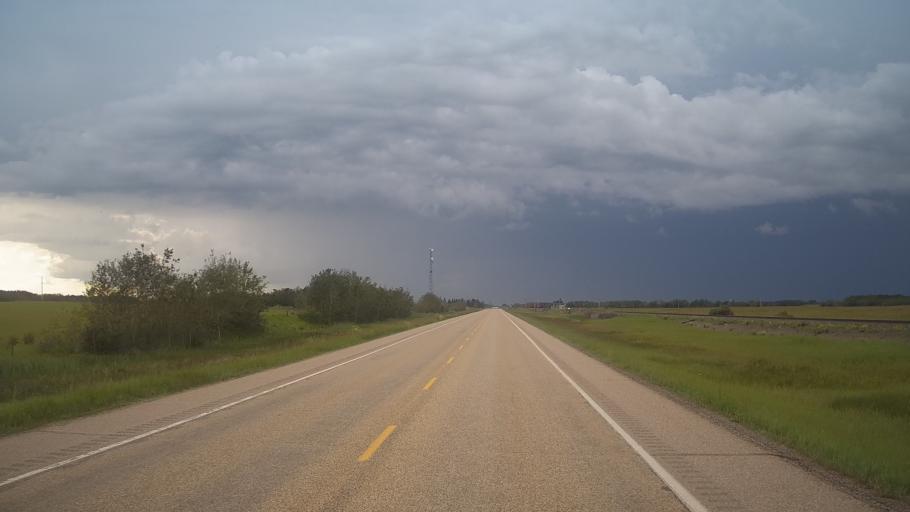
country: CA
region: Alberta
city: Tofield
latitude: 53.2668
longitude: -112.3595
